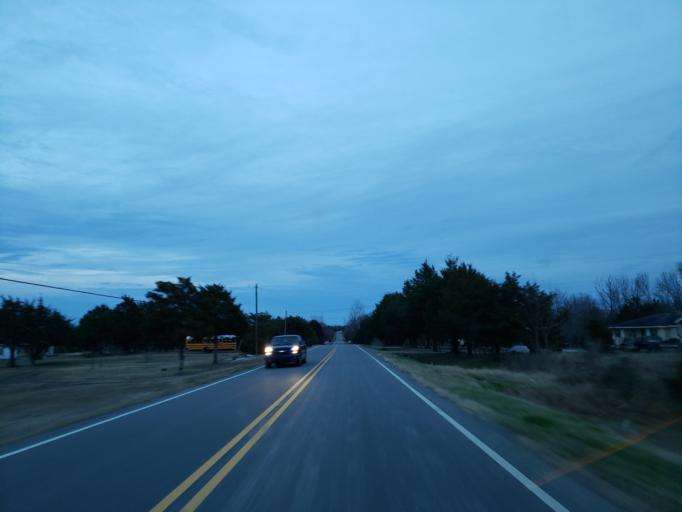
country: US
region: Alabama
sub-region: Sumter County
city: Livingston
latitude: 32.8098
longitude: -88.2282
